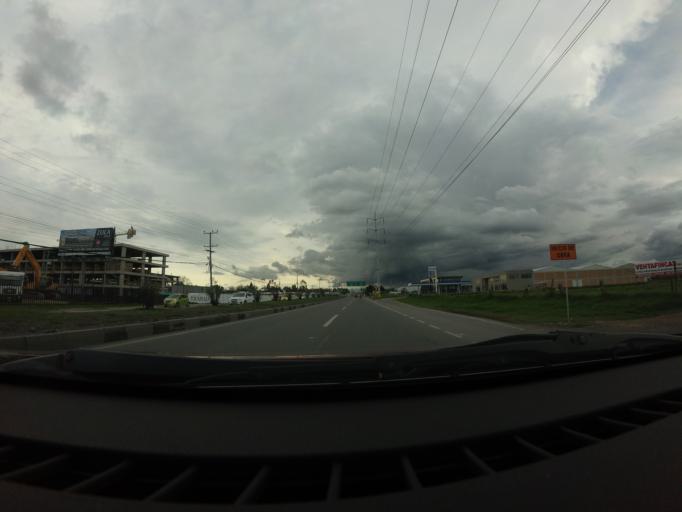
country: CO
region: Cundinamarca
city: Funza
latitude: 4.7550
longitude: -74.1512
